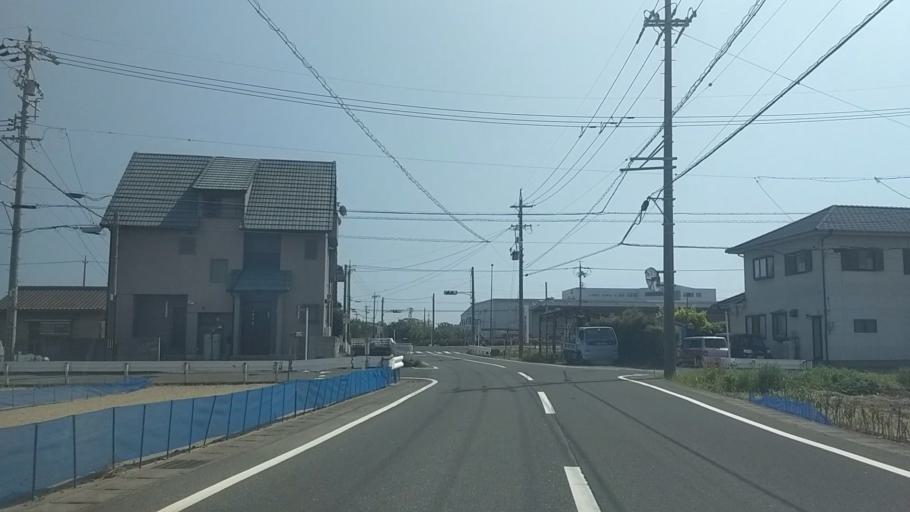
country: JP
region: Shizuoka
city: Hamamatsu
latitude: 34.6717
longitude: 137.7159
